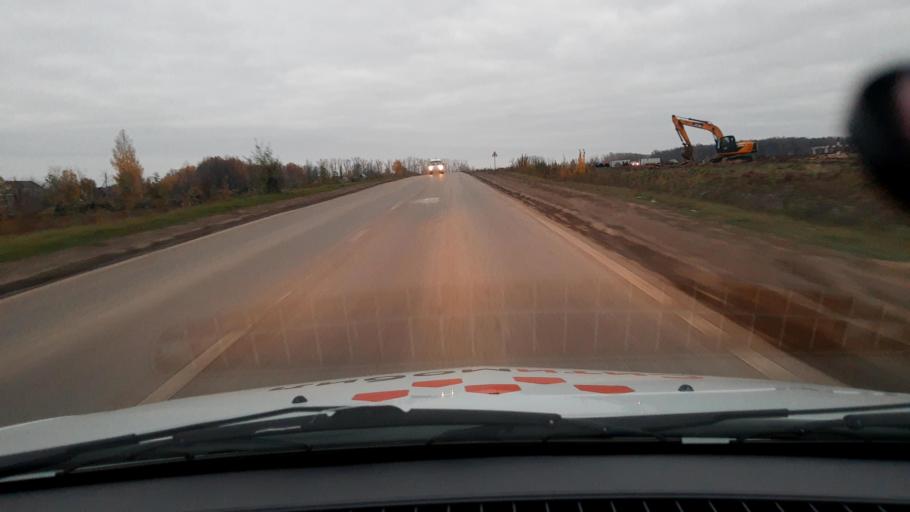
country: RU
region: Bashkortostan
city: Kabakovo
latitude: 54.6955
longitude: 56.1479
